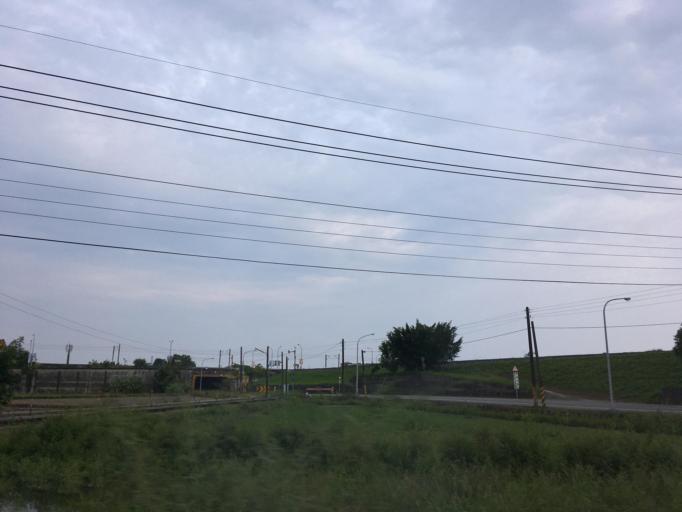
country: TW
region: Taiwan
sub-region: Yilan
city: Yilan
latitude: 24.7189
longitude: 121.7693
